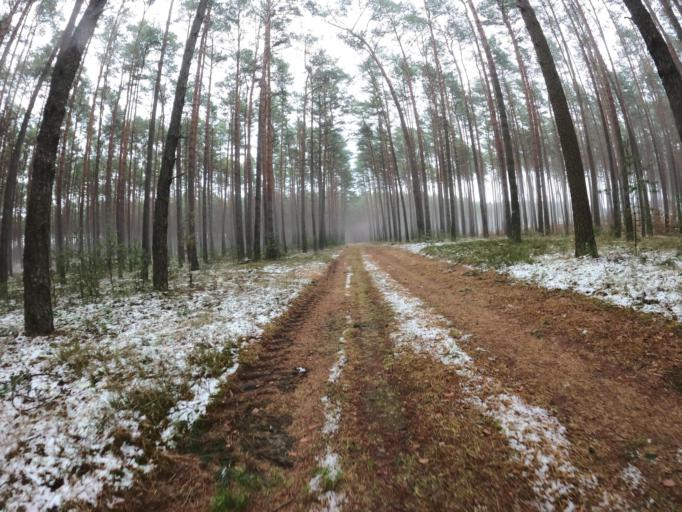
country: PL
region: Lubusz
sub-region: Powiat krosnienski
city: Maszewo
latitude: 52.2073
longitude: 14.9468
